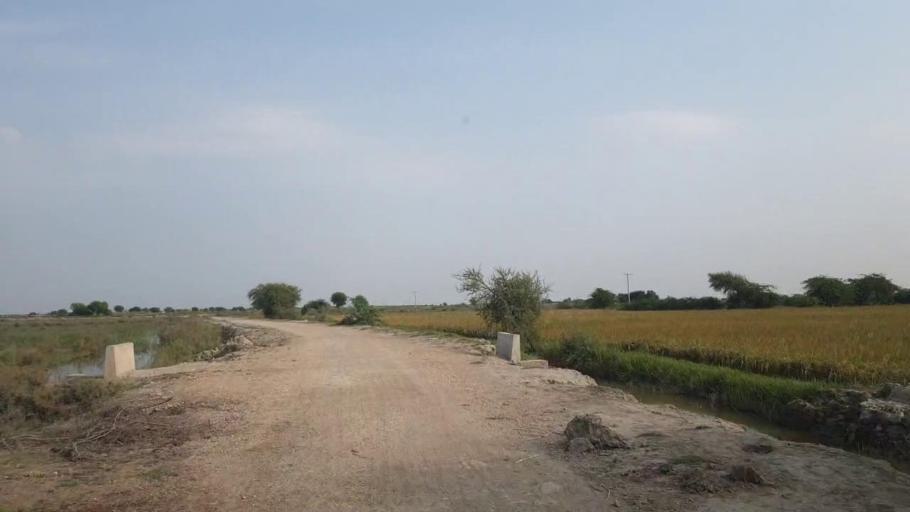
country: PK
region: Sindh
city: Kadhan
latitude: 24.4589
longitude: 68.8030
